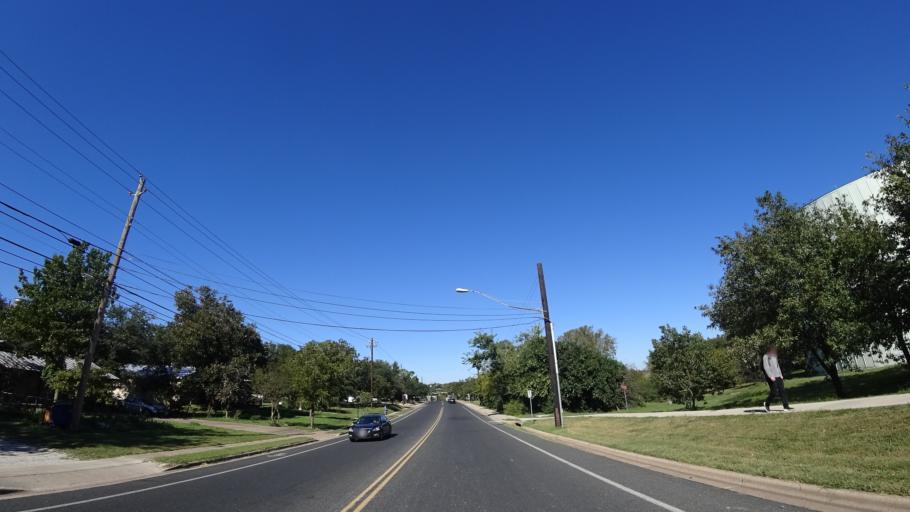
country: US
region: Texas
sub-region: Travis County
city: Austin
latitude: 30.2285
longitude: -97.7577
